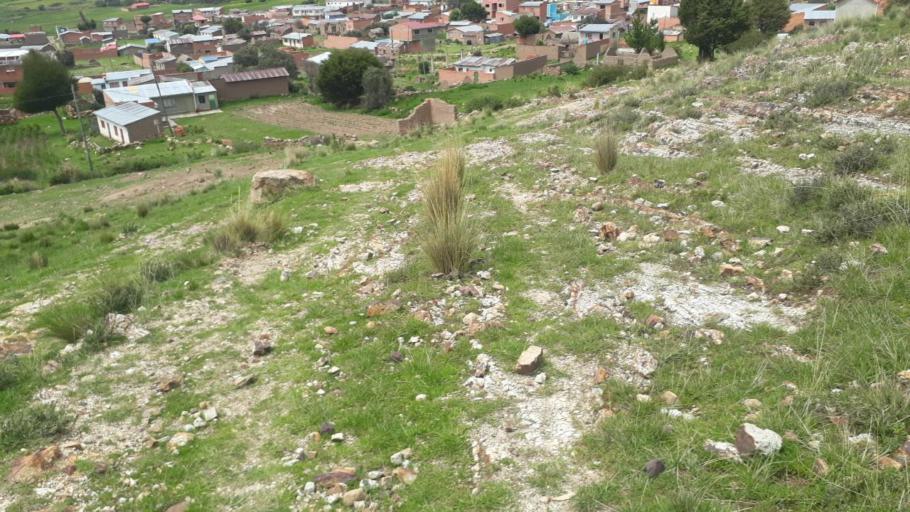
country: BO
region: La Paz
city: Batallas
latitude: -16.3441
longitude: -68.6370
